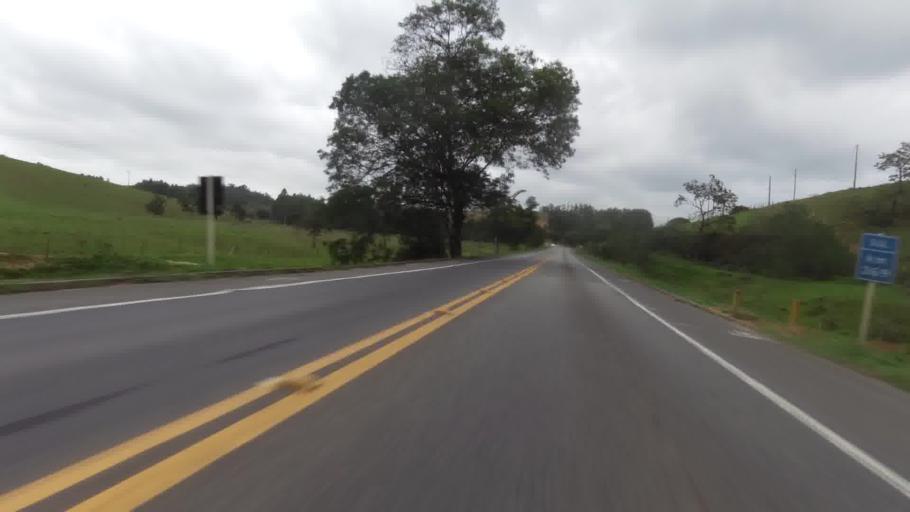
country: BR
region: Espirito Santo
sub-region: Iconha
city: Iconha
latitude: -20.7596
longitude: -40.7575
